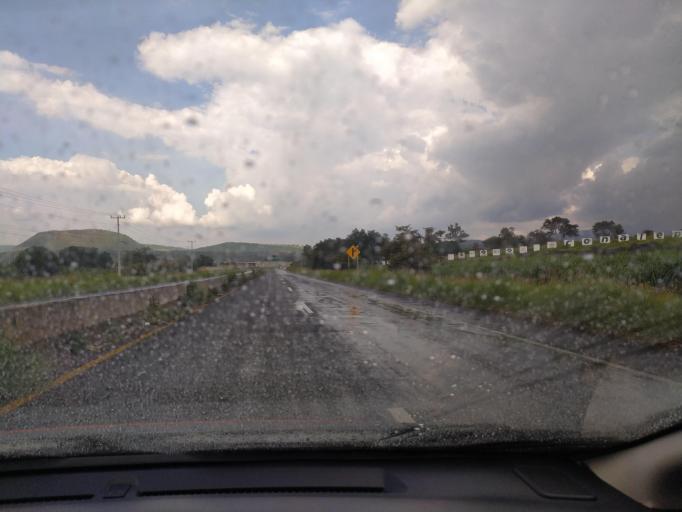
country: MX
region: Jalisco
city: Bellavista
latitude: 20.4214
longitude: -103.6130
